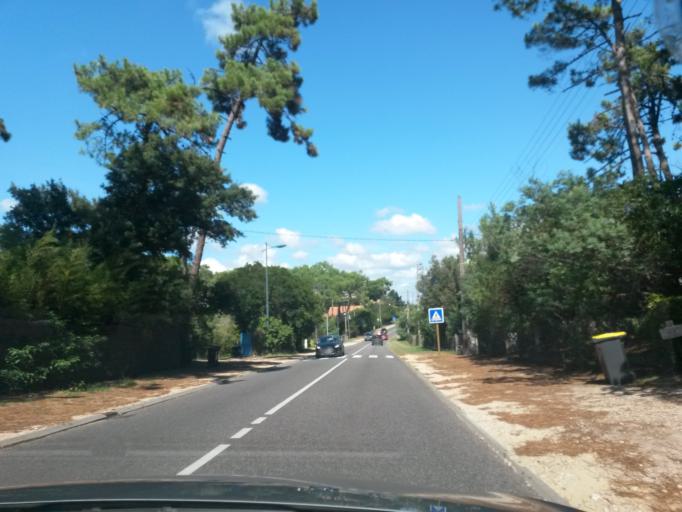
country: FR
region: Aquitaine
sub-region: Departement de la Gironde
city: Arcachon
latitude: 44.6960
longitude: -1.2327
